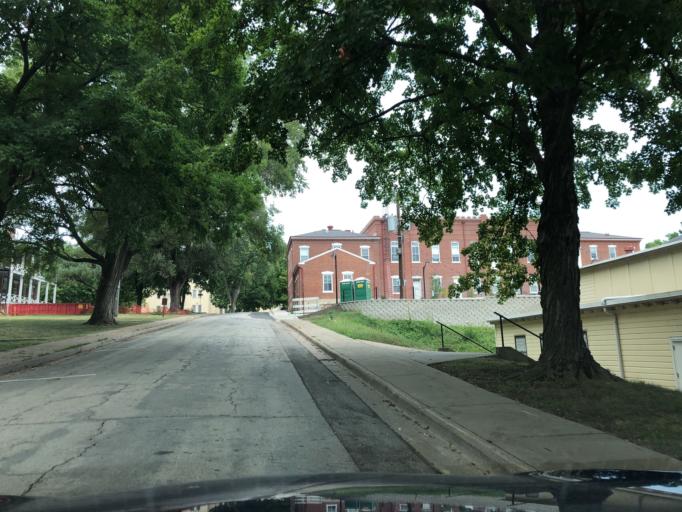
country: US
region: Kansas
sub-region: Leavenworth County
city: Leavenworth
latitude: 39.3497
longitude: -94.9152
